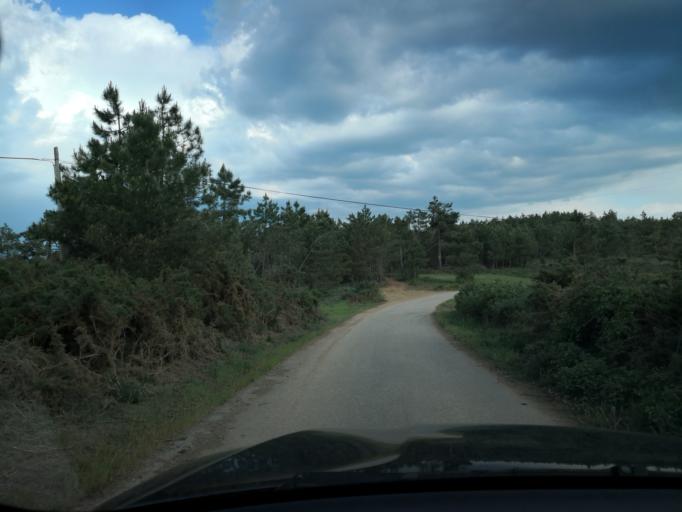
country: PT
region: Vila Real
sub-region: Sabrosa
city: Vilela
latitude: 41.2269
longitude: -7.6711
